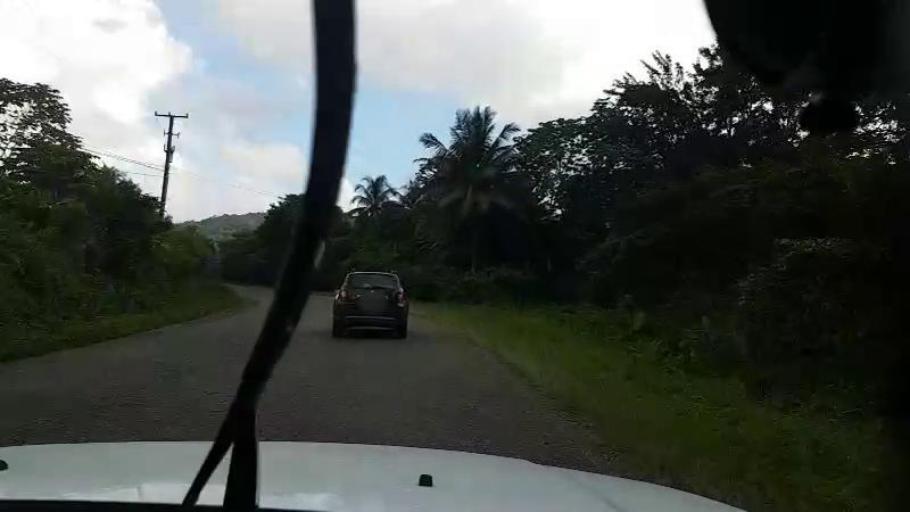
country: BZ
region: Stann Creek
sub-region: Dangriga
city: Dangriga
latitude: 17.0017
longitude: -88.4341
